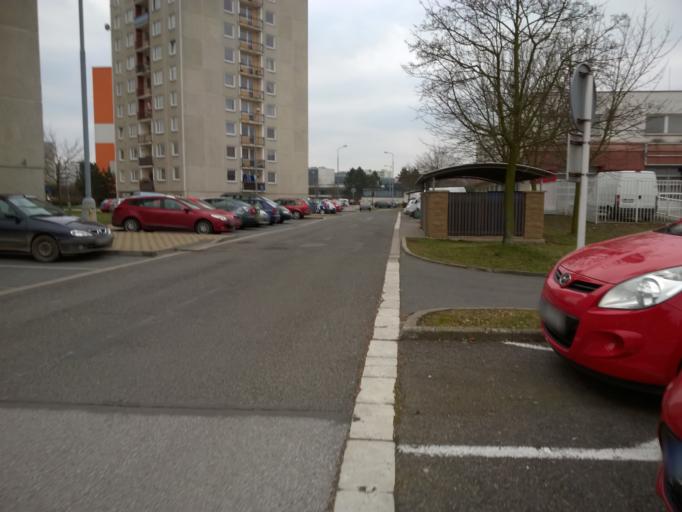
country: CZ
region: Pardubicky
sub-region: Okres Pardubice
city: Pardubice
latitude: 50.0528
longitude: 15.7700
